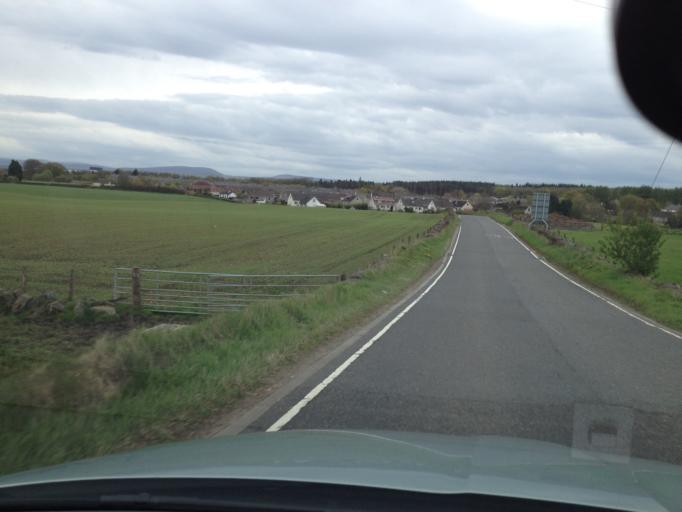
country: GB
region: Scotland
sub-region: West Lothian
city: Livingston
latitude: 55.9255
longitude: -3.5379
